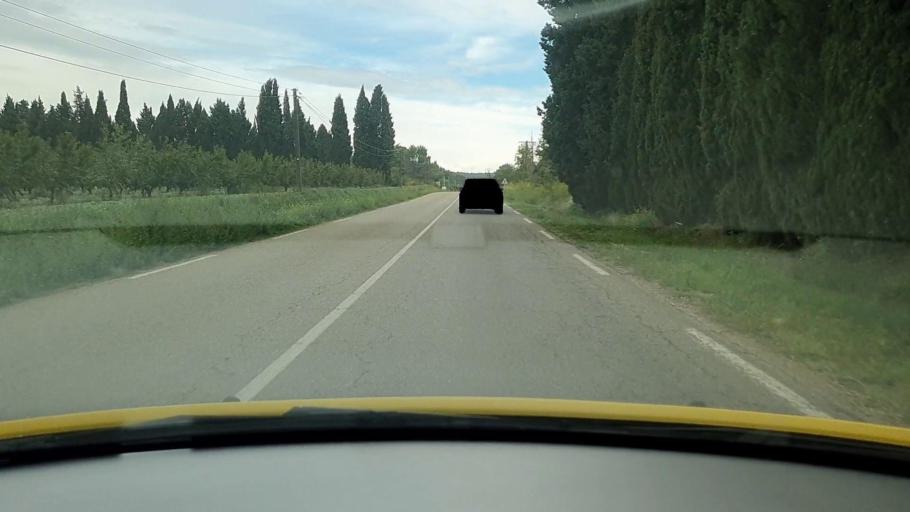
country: FR
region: Languedoc-Roussillon
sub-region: Departement du Gard
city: Saint-Gilles
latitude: 43.7130
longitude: 4.4570
